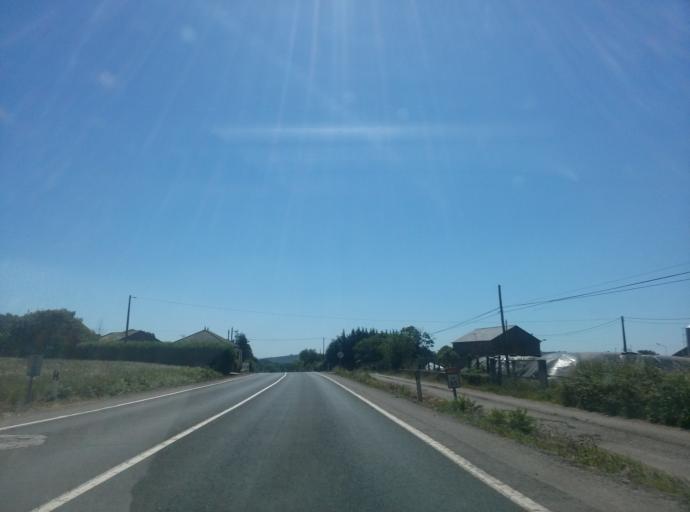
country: ES
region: Galicia
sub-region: Provincia de Lugo
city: Pol
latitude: 43.1879
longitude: -7.3443
